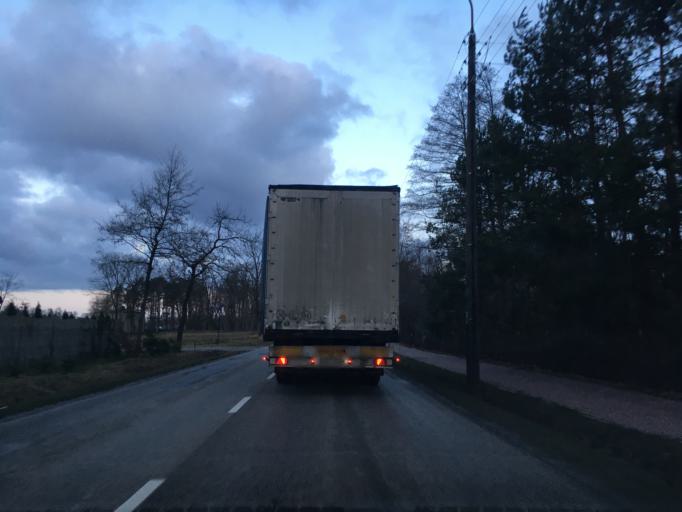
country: PL
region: Masovian Voivodeship
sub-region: Powiat grodziski
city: Milanowek
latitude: 52.0945
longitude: 20.6604
